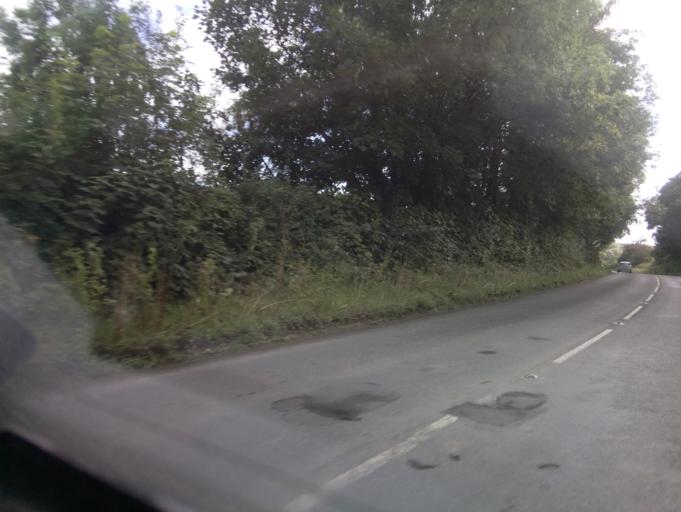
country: GB
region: England
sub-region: Devon
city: Ivybridge
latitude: 50.3576
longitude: -3.9216
